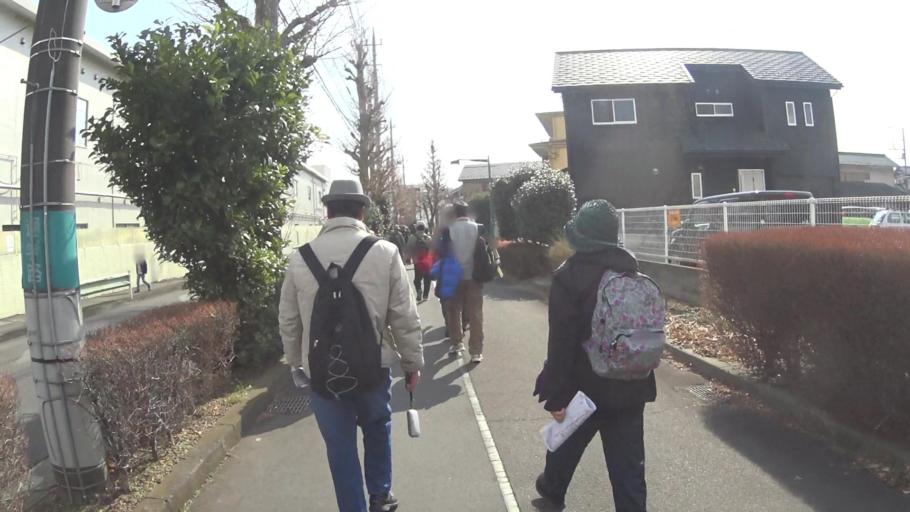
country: JP
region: Tokyo
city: Kokubunji
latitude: 35.6588
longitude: 139.4728
